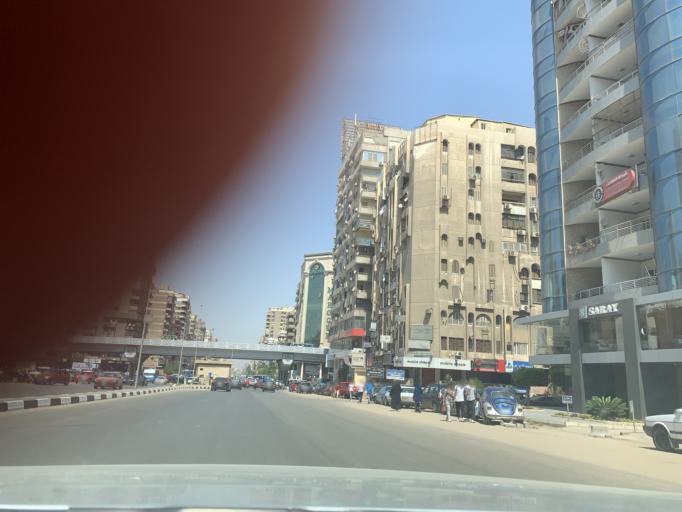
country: EG
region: Muhafazat al Qahirah
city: Cairo
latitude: 30.0532
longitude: 31.3465
